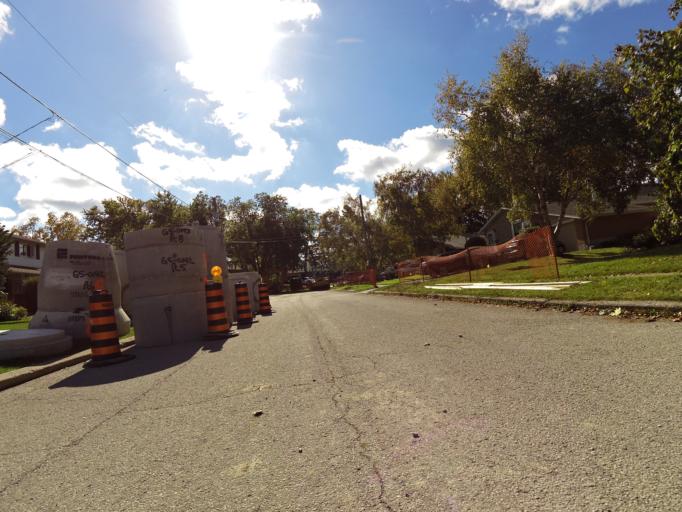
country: CA
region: Ontario
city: Ajax
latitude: 43.8197
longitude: -79.0988
